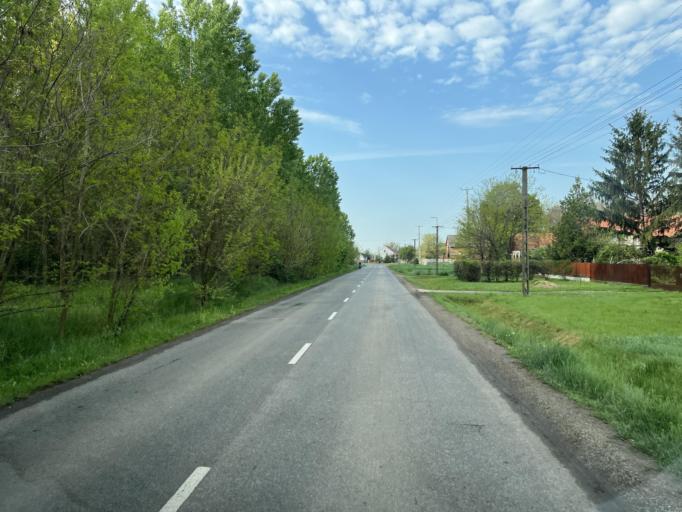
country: HU
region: Pest
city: Abony
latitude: 47.2065
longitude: 20.0101
